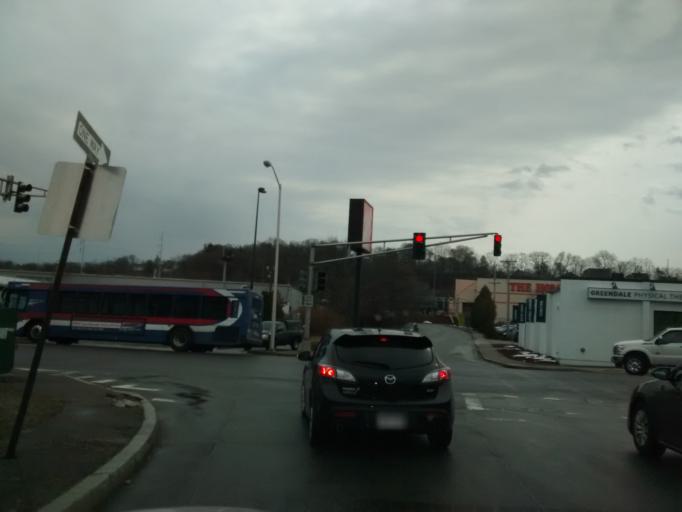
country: US
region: Massachusetts
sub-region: Worcester County
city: Worcester
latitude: 42.2923
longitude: -71.8030
